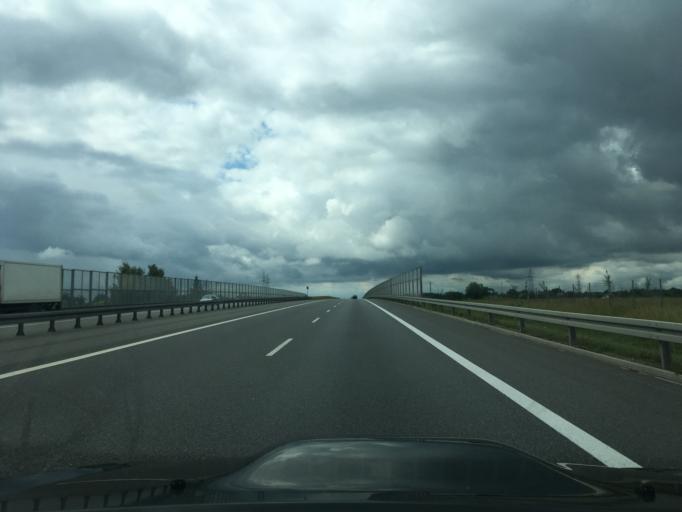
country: PL
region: Lublin Voivodeship
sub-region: Powiat lubelski
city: Jakubowice Murowane
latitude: 51.2854
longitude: 22.6268
